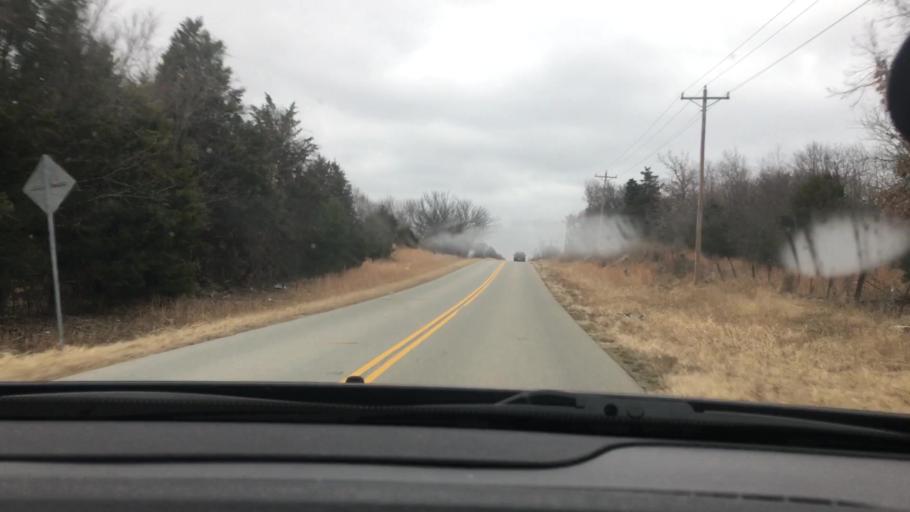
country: US
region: Oklahoma
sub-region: Atoka County
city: Atoka
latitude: 34.3322
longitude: -96.0754
